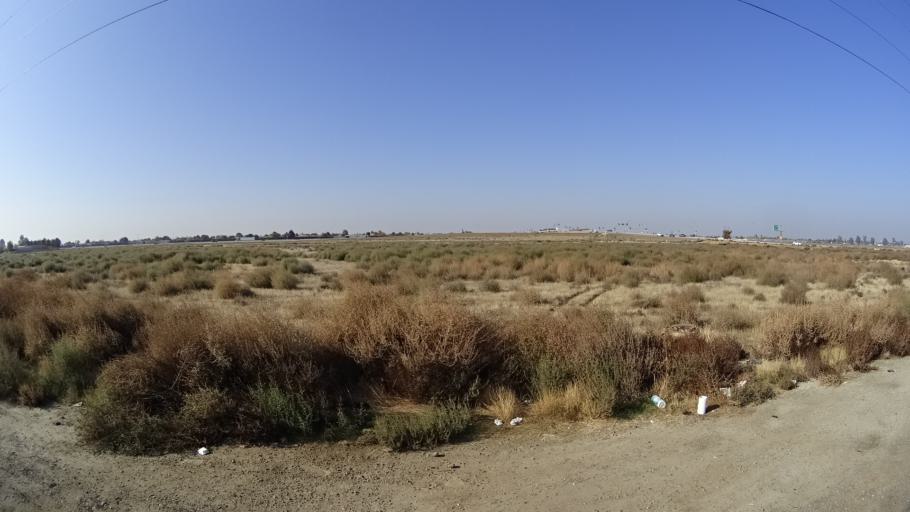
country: US
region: California
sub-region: Kern County
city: Greenfield
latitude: 35.2801
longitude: -119.0213
